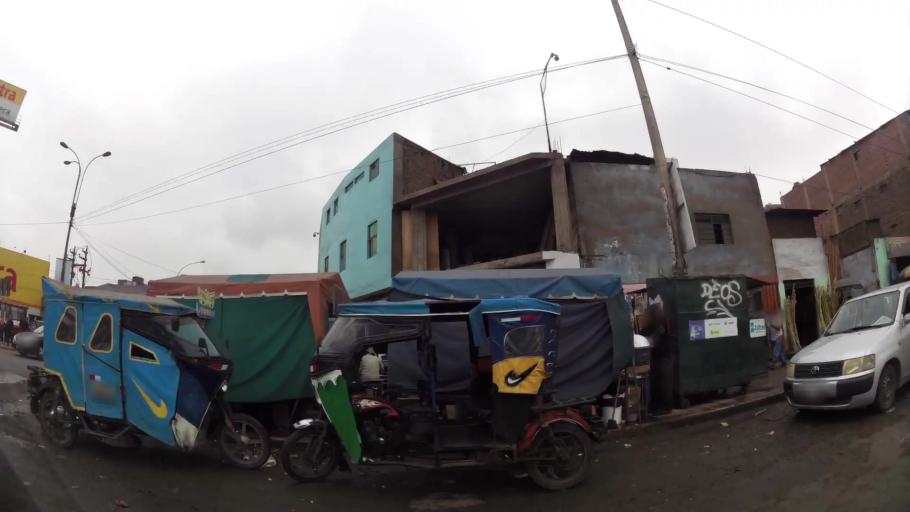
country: PE
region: Lima
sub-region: Lima
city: San Luis
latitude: -12.0596
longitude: -77.0078
